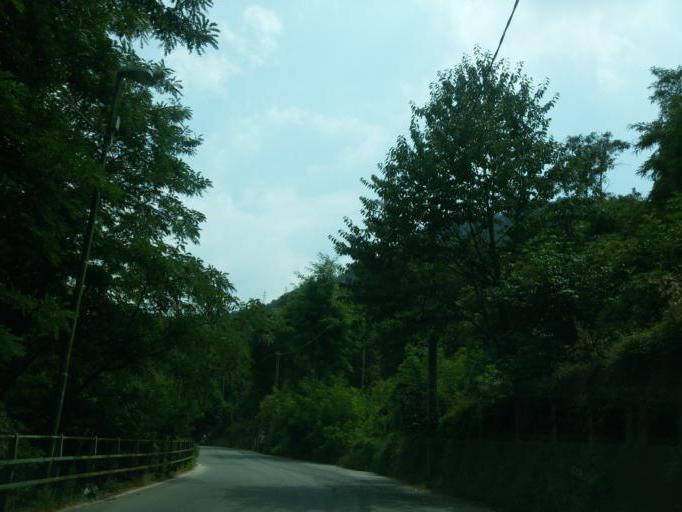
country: IT
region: Liguria
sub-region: Provincia di Genova
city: Piccarello
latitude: 44.4422
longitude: 8.9919
